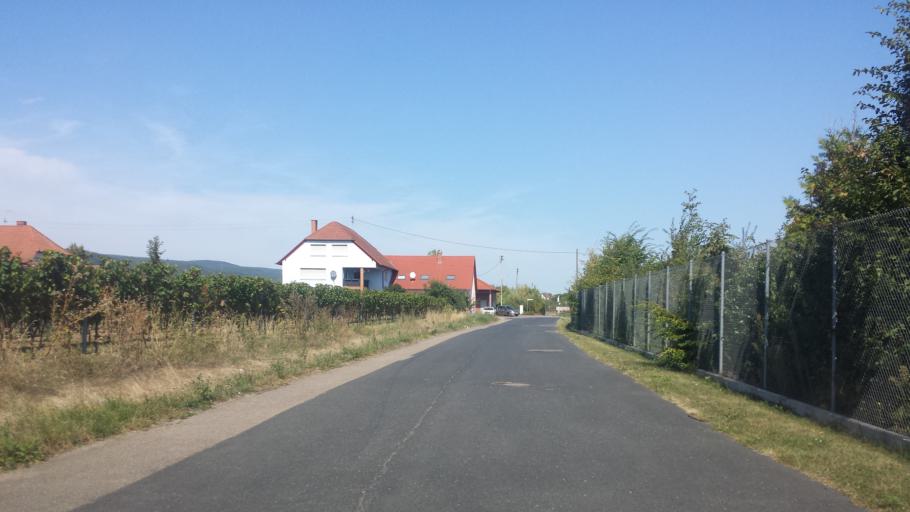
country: DE
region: Rheinland-Pfalz
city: Neustadt
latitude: 49.3574
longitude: 8.1723
